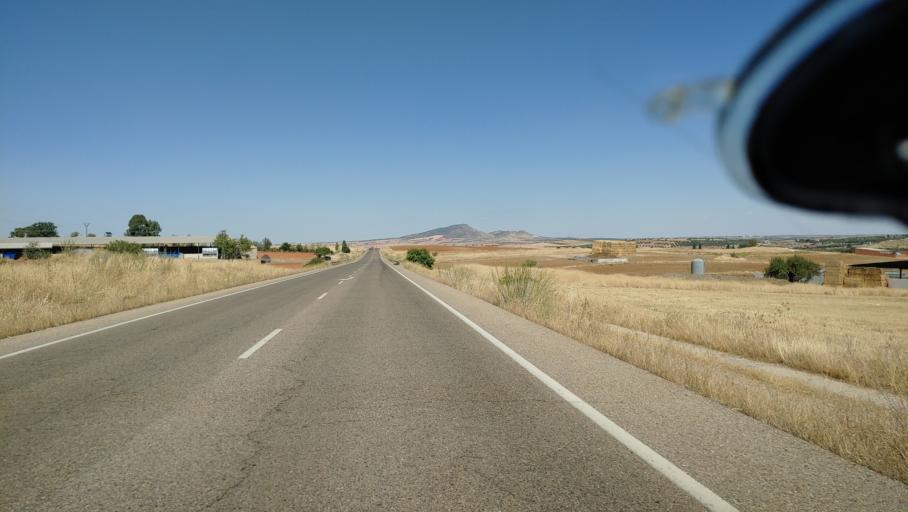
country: ES
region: Castille-La Mancha
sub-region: Province of Toledo
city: Pulgar
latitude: 39.6825
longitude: -4.1714
